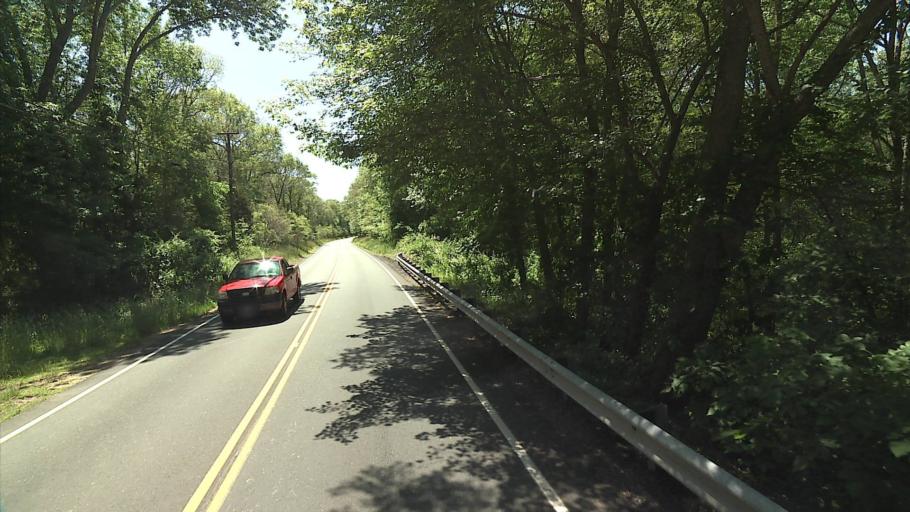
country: US
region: Connecticut
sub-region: Windham County
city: Plainfield
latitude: 41.6251
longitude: -71.8463
